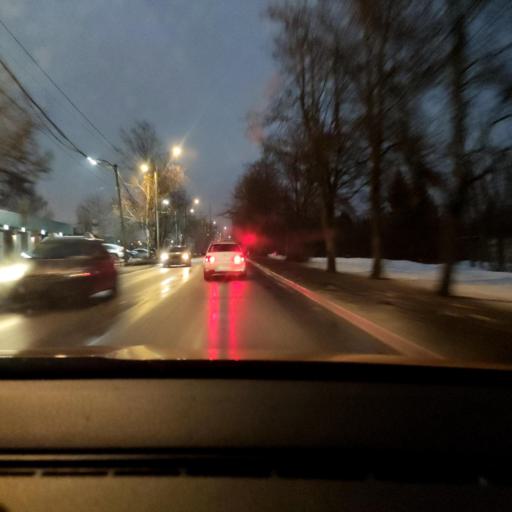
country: RU
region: Moskovskaya
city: Mosrentgen
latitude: 55.6187
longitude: 37.4569
